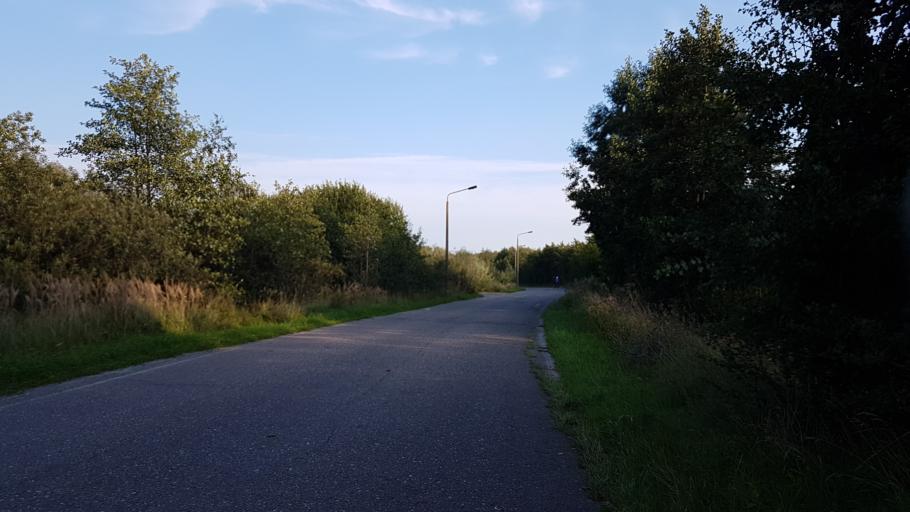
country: DE
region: Mecklenburg-Vorpommern
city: Sagard
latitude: 54.4963
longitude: 13.5519
